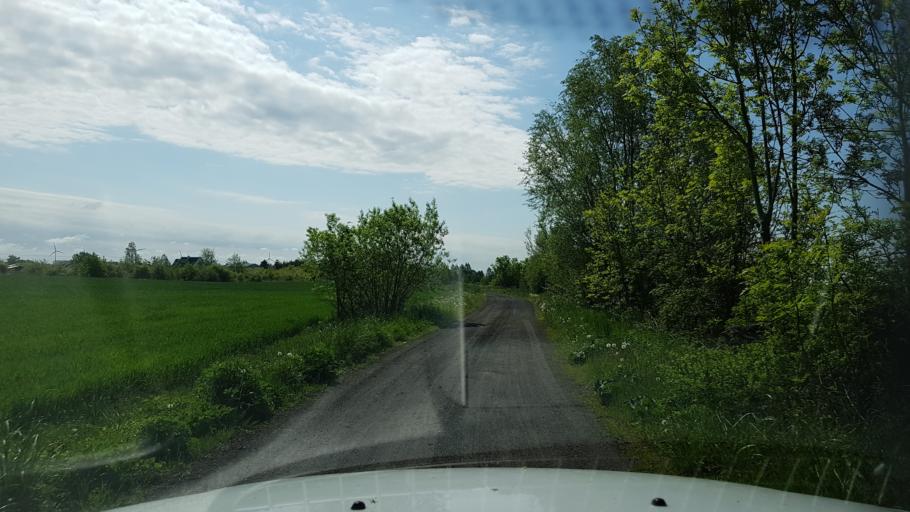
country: PL
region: West Pomeranian Voivodeship
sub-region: Powiat kolobrzeski
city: Ustronie Morskie
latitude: 54.2208
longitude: 15.8288
